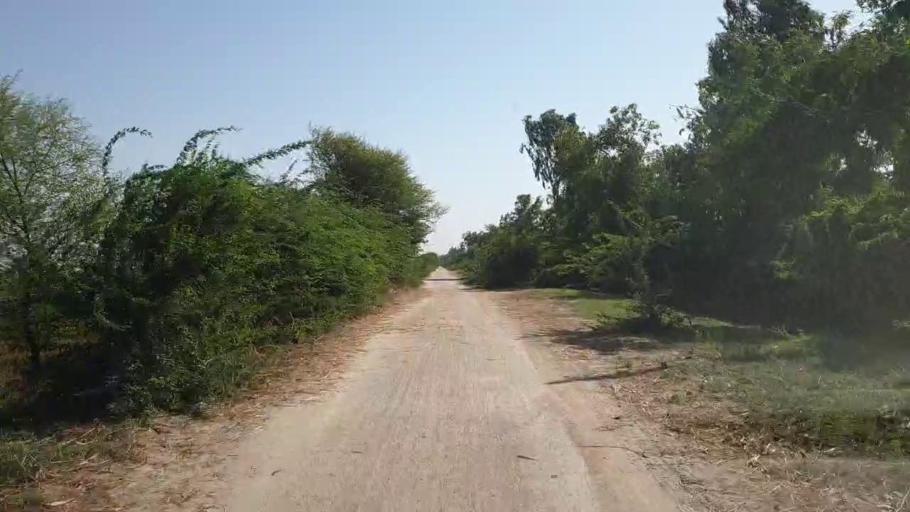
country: PK
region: Sindh
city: Tando Bago
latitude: 24.6544
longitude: 68.9814
